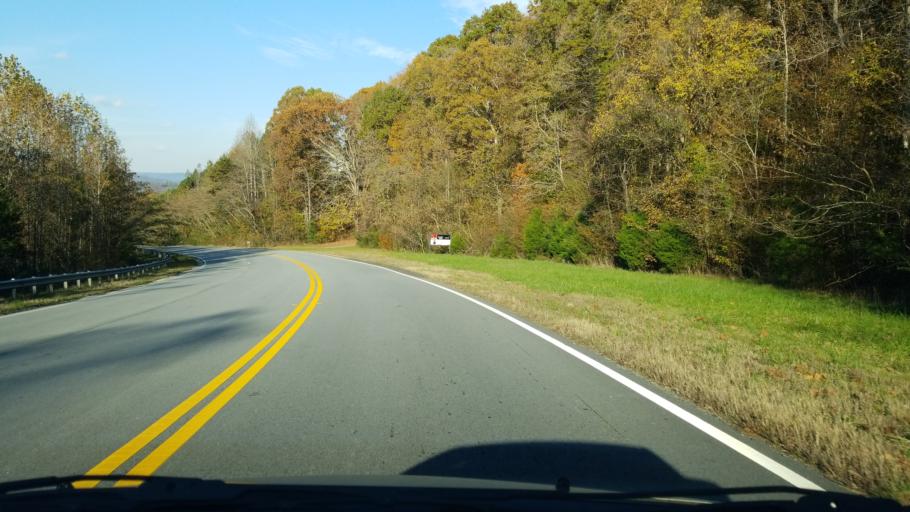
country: US
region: Georgia
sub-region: Dade County
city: Trenton
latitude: 34.8544
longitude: -85.4952
